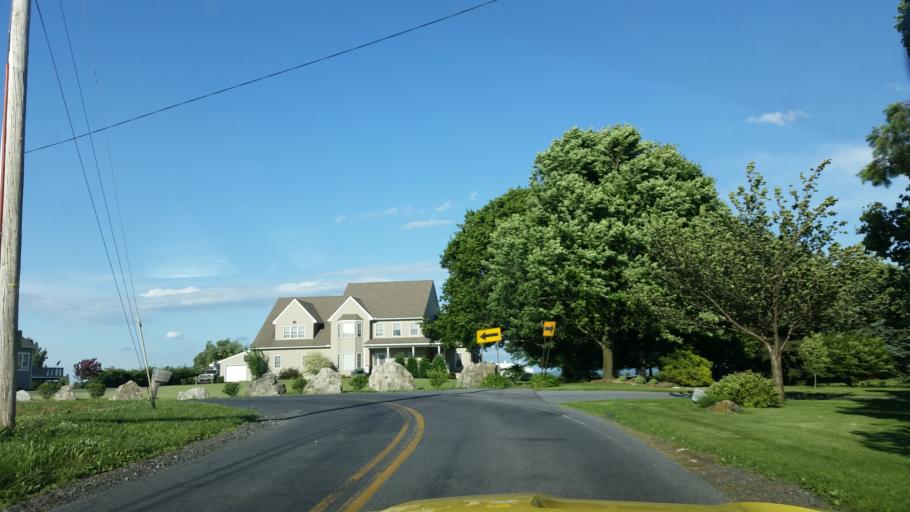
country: US
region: Pennsylvania
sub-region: Lebanon County
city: Avon
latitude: 40.3274
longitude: -76.3618
